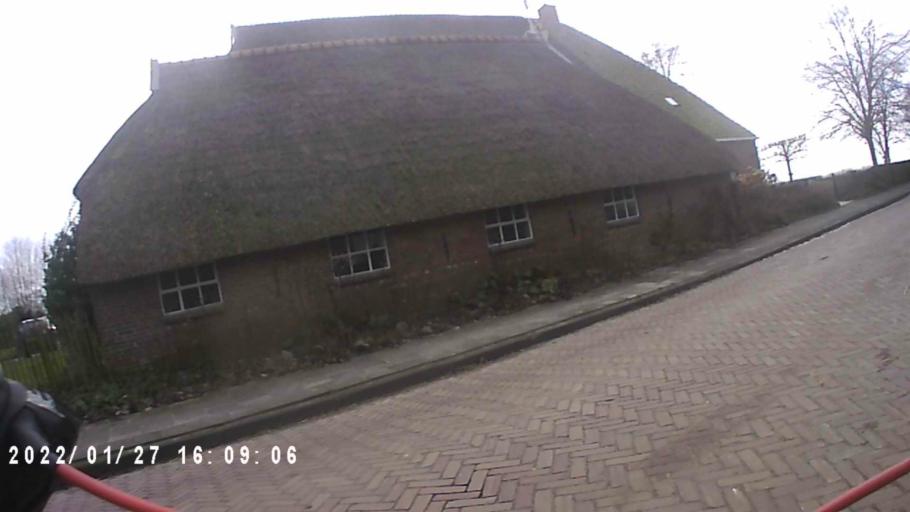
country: NL
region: Friesland
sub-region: Gemeente Dongeradeel
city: Anjum
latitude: 53.3807
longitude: 6.0845
